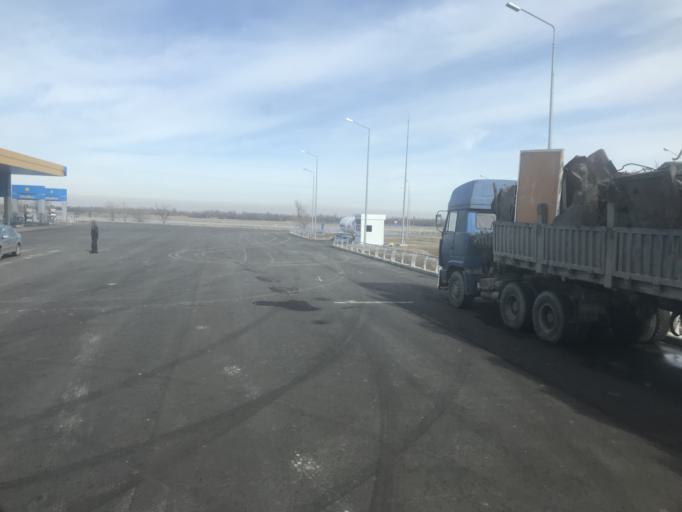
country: KZ
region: Zhambyl
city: Sarykemer
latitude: 43.0079
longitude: 71.7853
